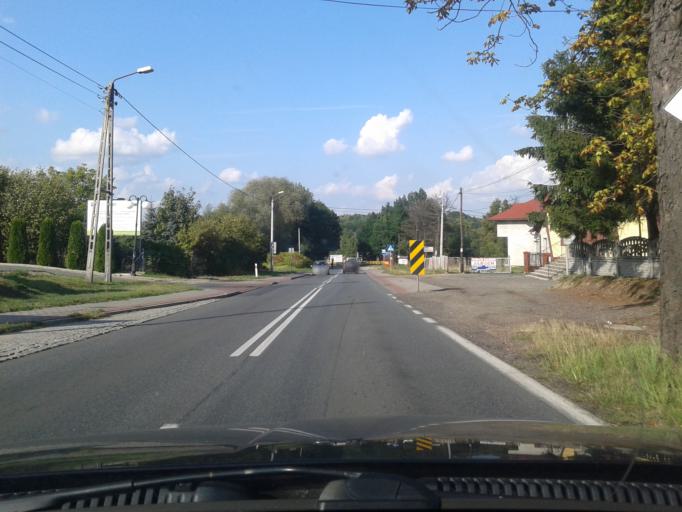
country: PL
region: Silesian Voivodeship
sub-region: Powiat wodzislawski
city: Turza Slaska
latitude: 49.9849
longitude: 18.4538
